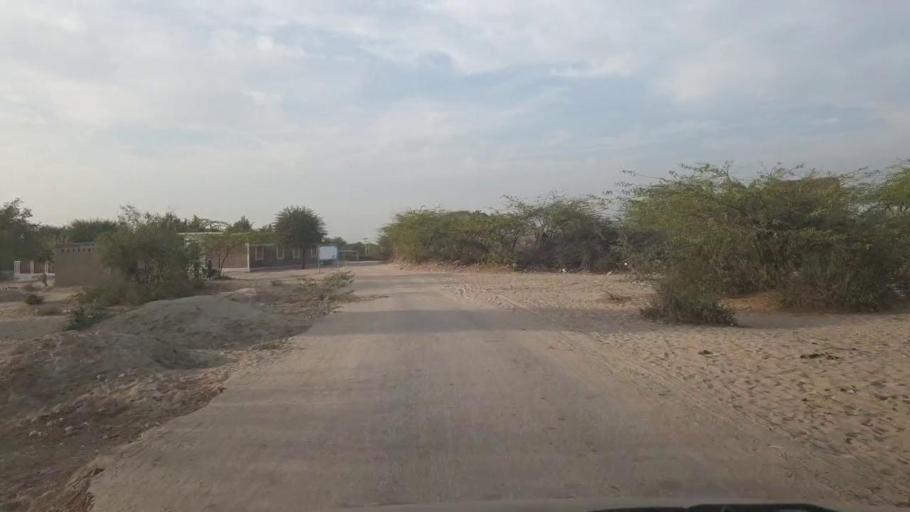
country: PK
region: Sindh
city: Nabisar
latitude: 25.1484
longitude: 69.6706
